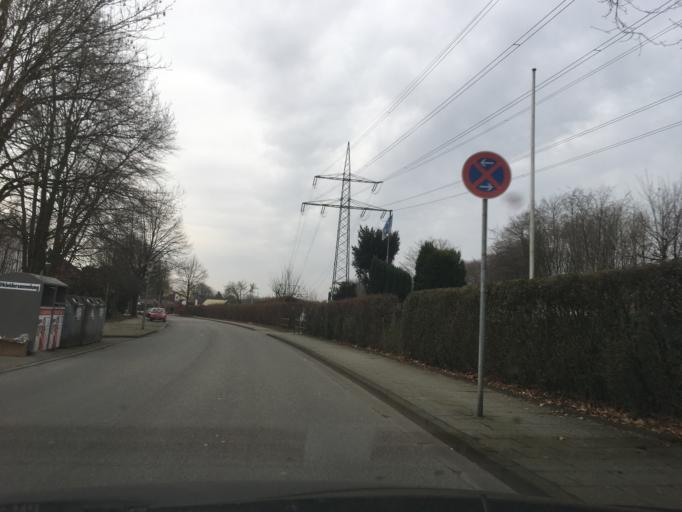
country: DE
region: North Rhine-Westphalia
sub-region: Regierungsbezirk Munster
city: Gladbeck
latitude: 51.5510
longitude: 7.0158
